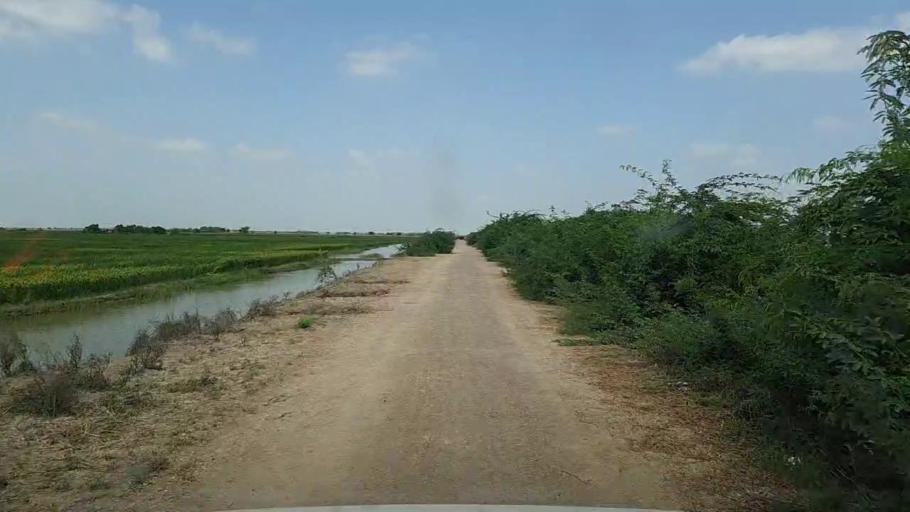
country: PK
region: Sindh
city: Kario
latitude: 24.6787
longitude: 68.5879
